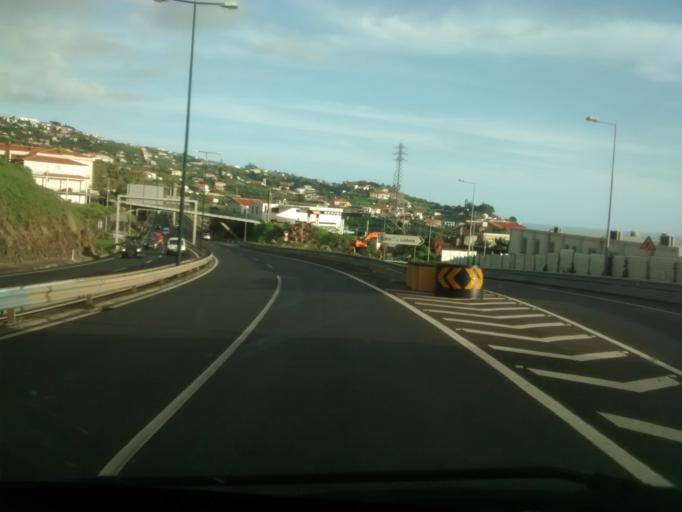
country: PT
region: Madeira
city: Camara de Lobos
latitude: 32.6560
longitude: -16.9680
